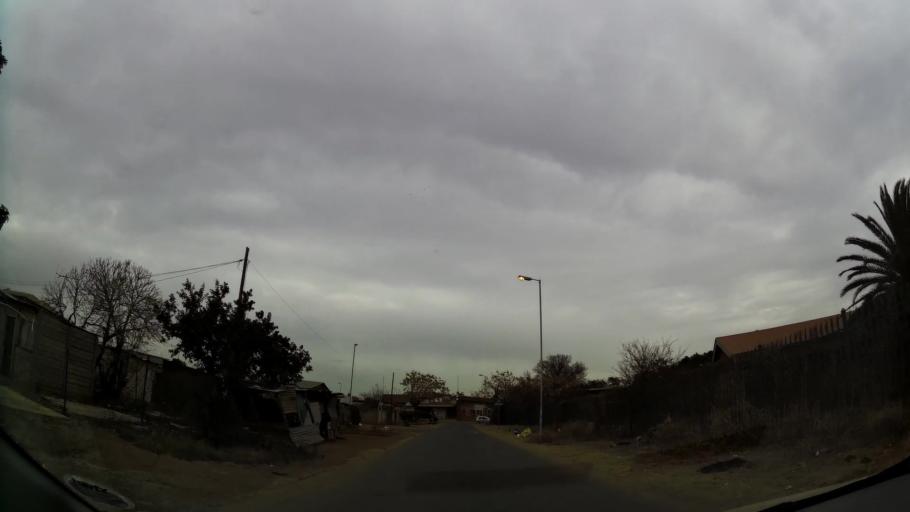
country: ZA
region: Gauteng
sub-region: City of Tshwane Metropolitan Municipality
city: Pretoria
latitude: -25.7113
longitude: 28.3564
